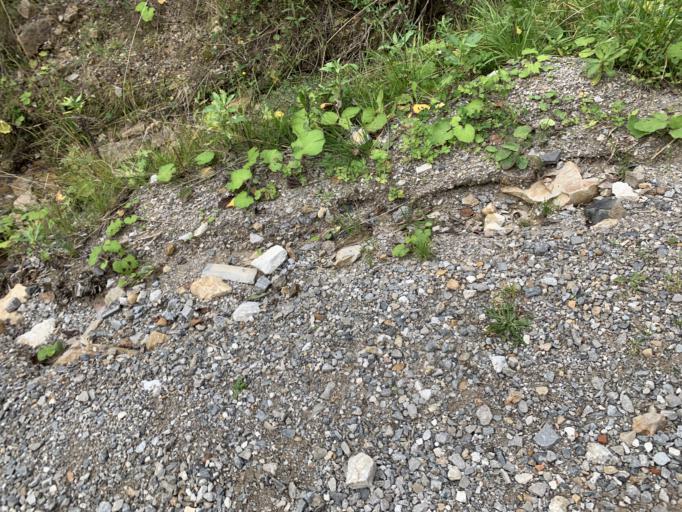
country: RU
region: Perm
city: Gubakha
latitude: 58.8405
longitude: 57.5732
